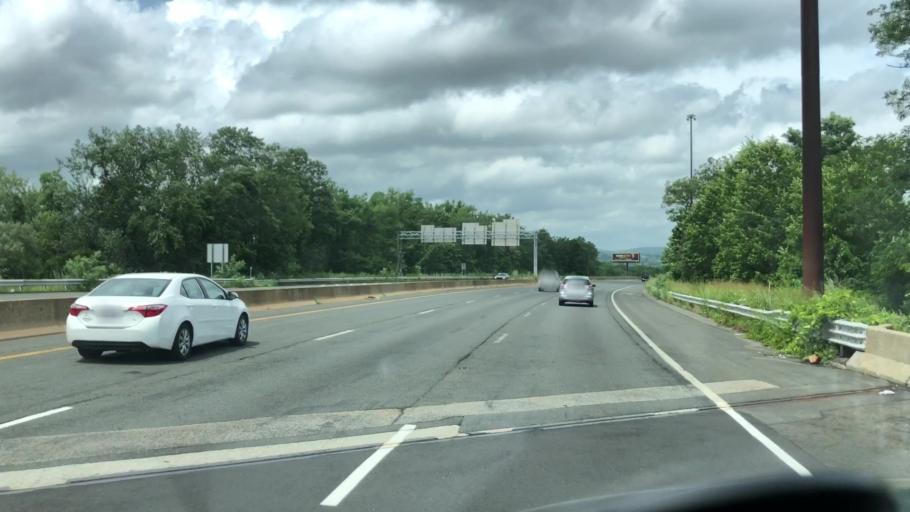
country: US
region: Massachusetts
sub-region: Hampden County
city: Chicopee
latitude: 42.1412
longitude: -72.6127
